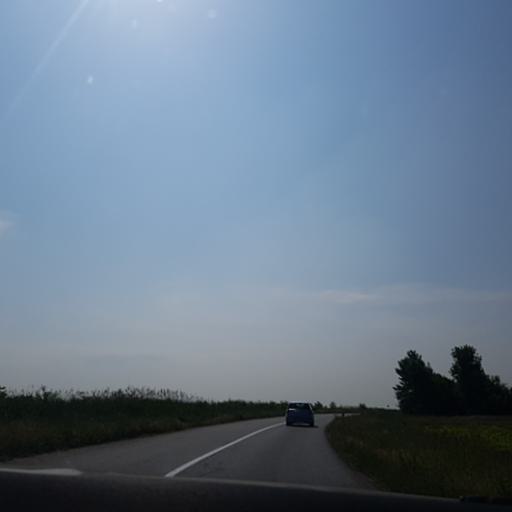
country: RS
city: Neuzina
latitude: 45.3408
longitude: 20.7198
